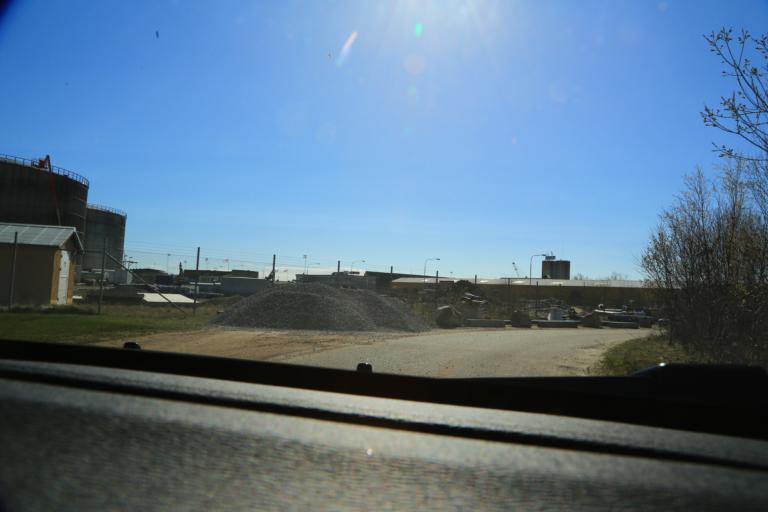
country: SE
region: Halland
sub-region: Varbergs Kommun
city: Varberg
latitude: 57.1181
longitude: 12.2503
